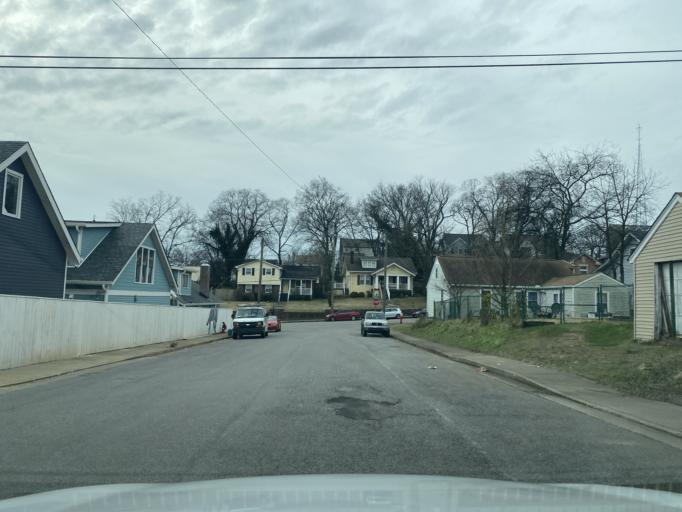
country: US
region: Tennessee
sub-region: Davidson County
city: Nashville
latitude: 36.1343
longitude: -86.7871
